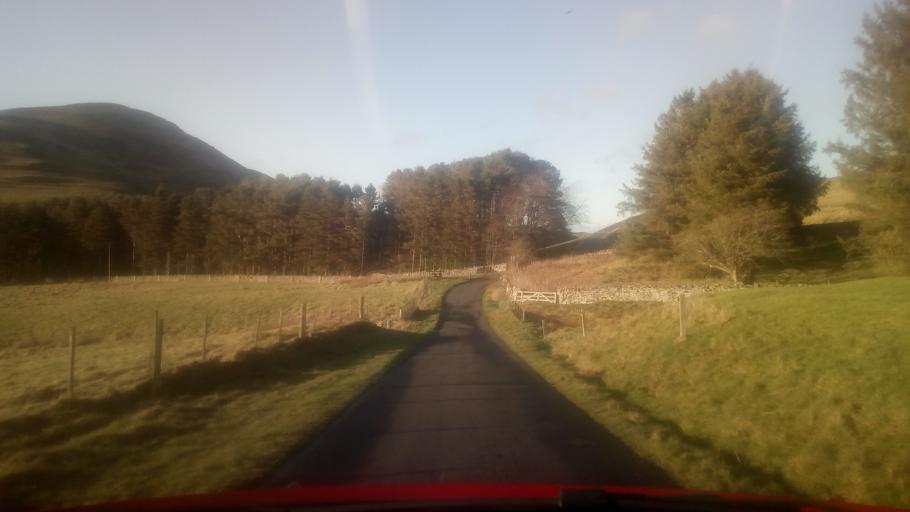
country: GB
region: Scotland
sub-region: The Scottish Borders
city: Kelso
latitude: 55.4374
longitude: -2.3635
